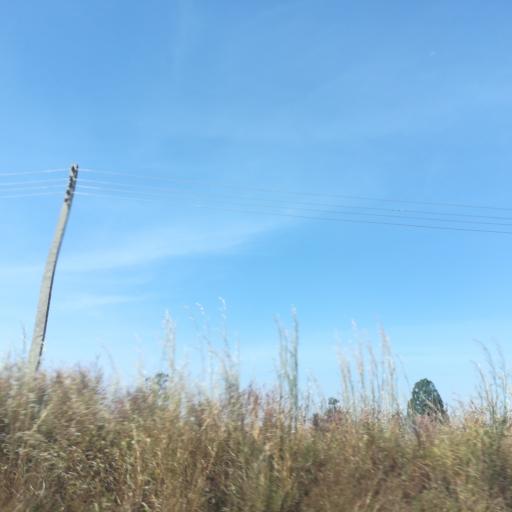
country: NG
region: Plateau
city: Bukuru
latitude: 9.7730
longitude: 8.8872
